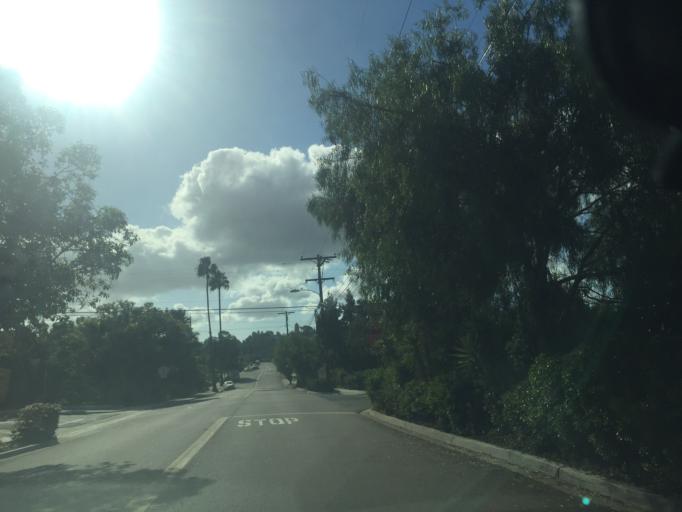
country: US
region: California
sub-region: San Diego County
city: La Mesa
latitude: 32.7891
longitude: -117.0939
